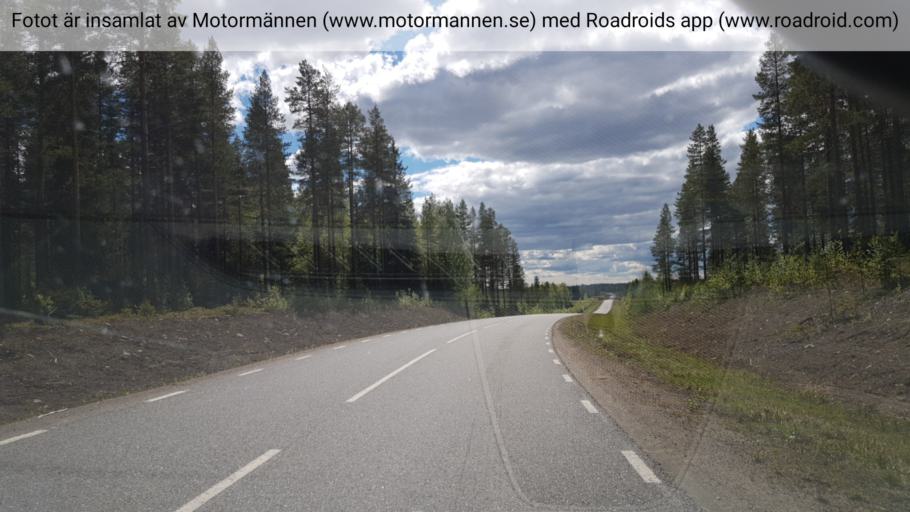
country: SE
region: Vaesterbotten
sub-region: Skelleftea Kommun
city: Langsele
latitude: 64.6801
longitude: 20.0291
